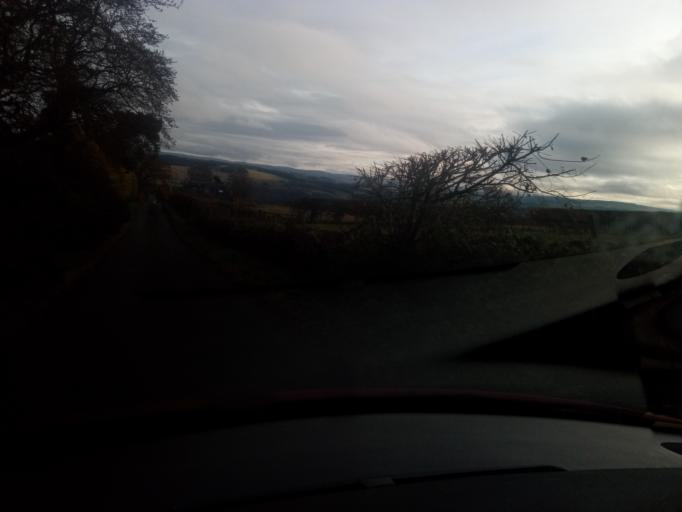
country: GB
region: Scotland
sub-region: The Scottish Borders
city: Jedburgh
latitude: 55.4795
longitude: -2.5703
